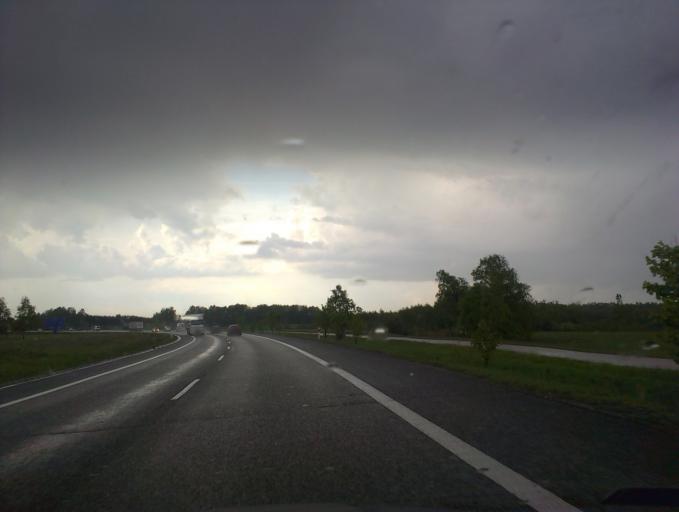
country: PL
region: Masovian Voivodeship
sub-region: Powiat zyrardowski
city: Mszczonow
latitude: 51.9907
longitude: 20.5095
